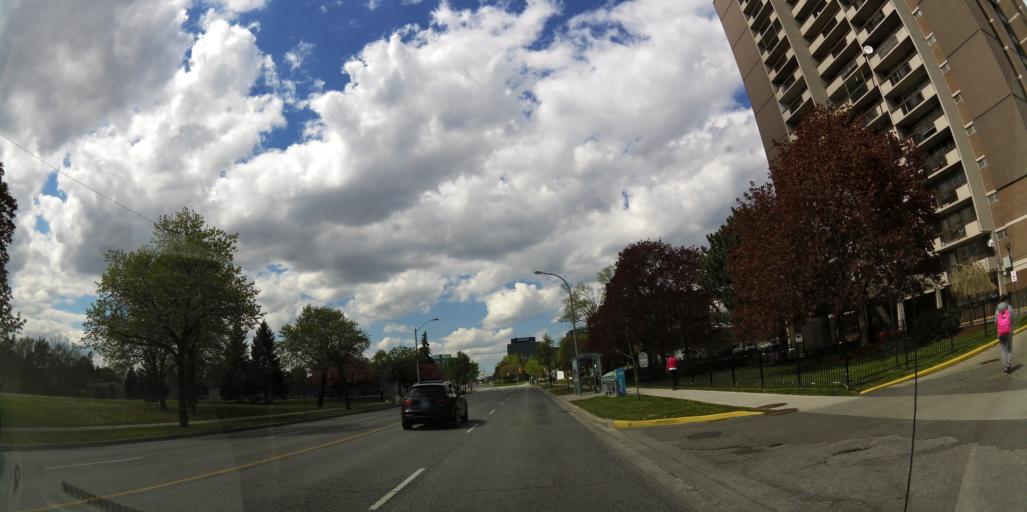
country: CA
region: Ontario
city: Etobicoke
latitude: 43.6406
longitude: -79.5652
